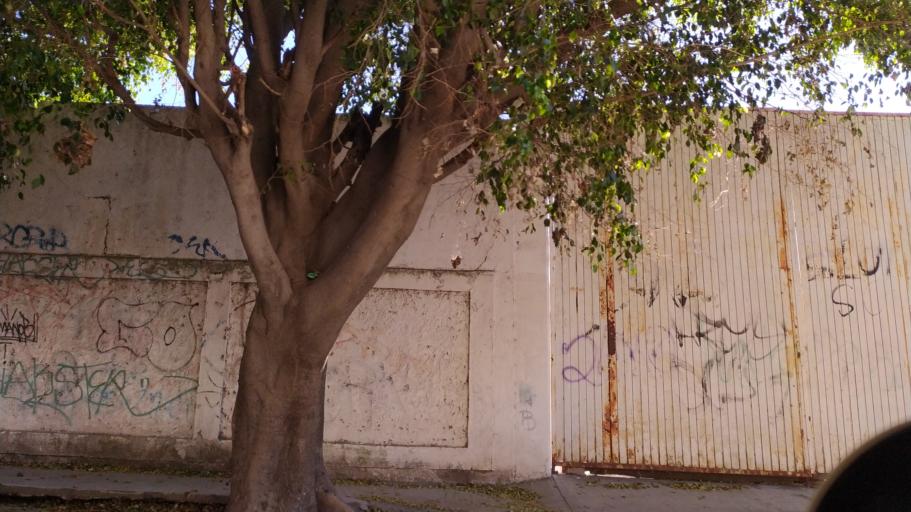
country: MX
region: Jalisco
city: Guadalajara
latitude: 20.6749
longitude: -103.4478
